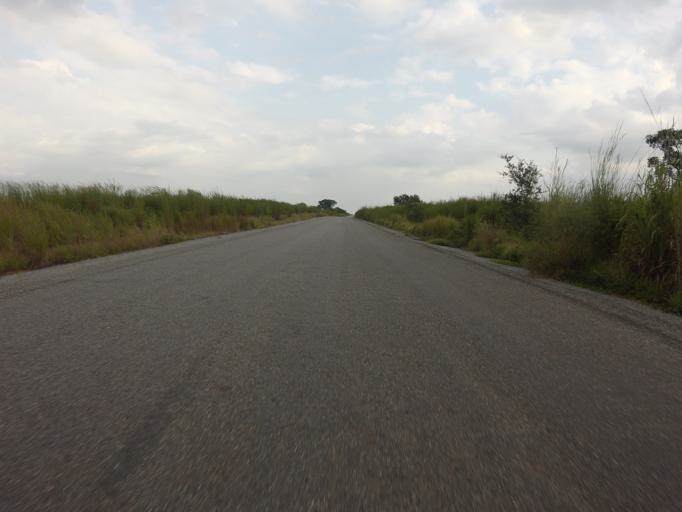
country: GH
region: Volta
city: Ho
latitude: 6.4201
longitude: 0.5197
